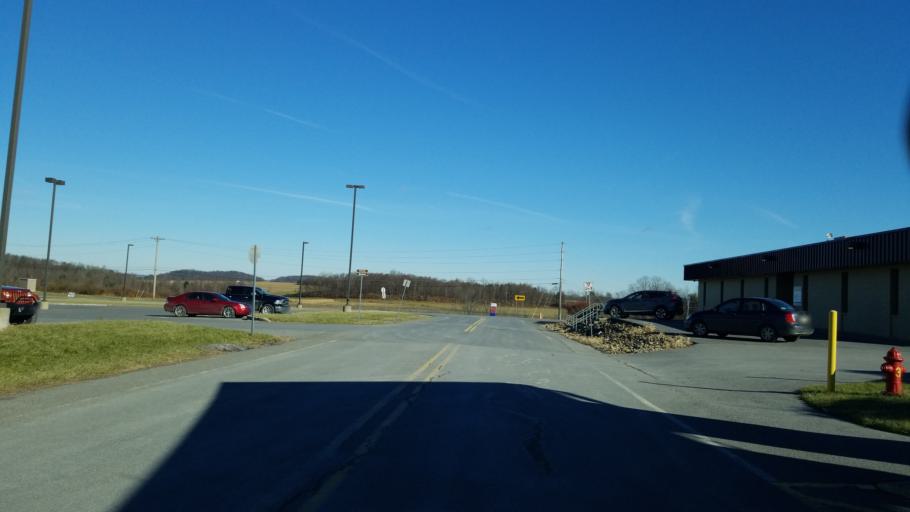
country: US
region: Pennsylvania
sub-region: Jefferson County
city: Reynoldsville
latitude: 41.1833
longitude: -78.8926
